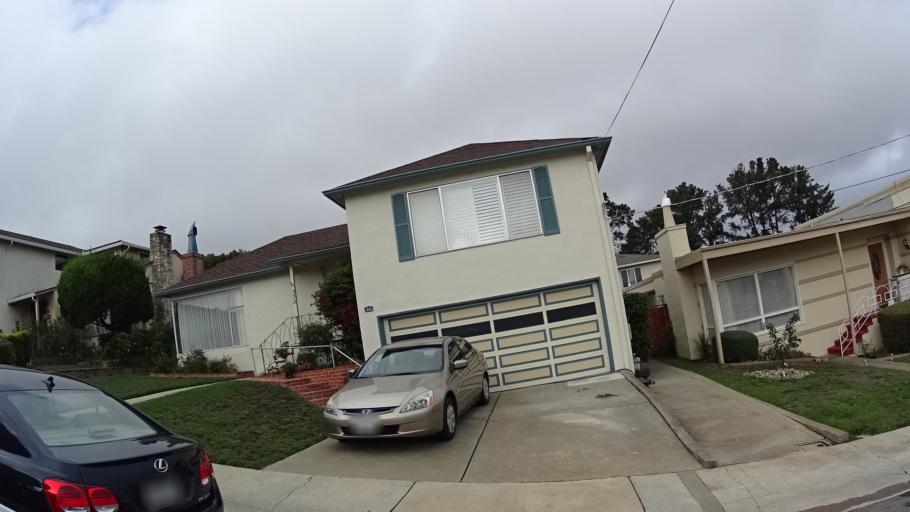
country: US
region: California
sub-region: San Mateo County
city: Millbrae
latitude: 37.6081
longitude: -122.4046
